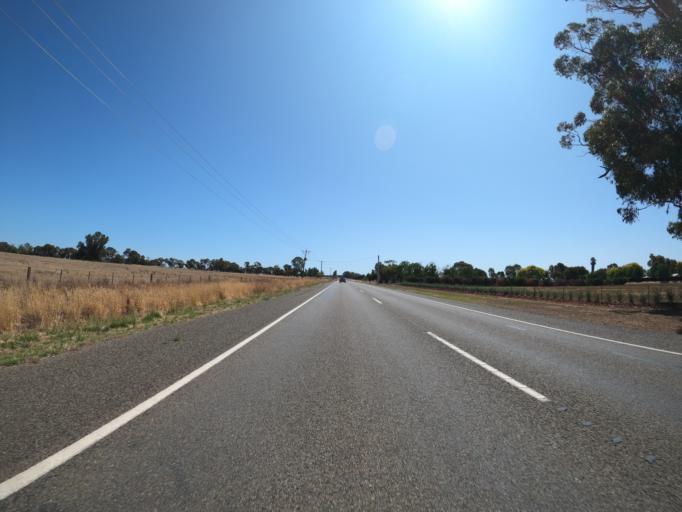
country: AU
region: Victoria
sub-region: Moira
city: Yarrawonga
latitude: -36.0266
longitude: 146.0867
